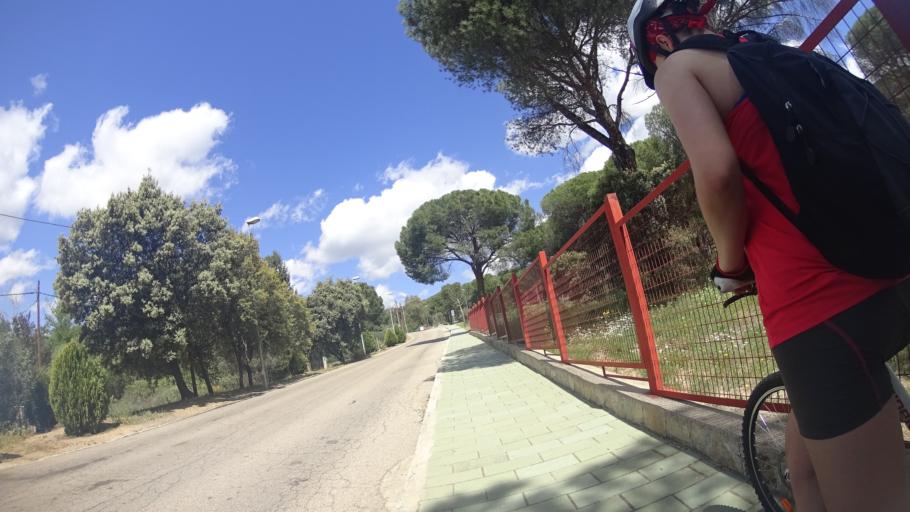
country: ES
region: Madrid
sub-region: Provincia de Madrid
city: Pelayos de la Presa
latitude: 40.3632
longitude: -4.3304
